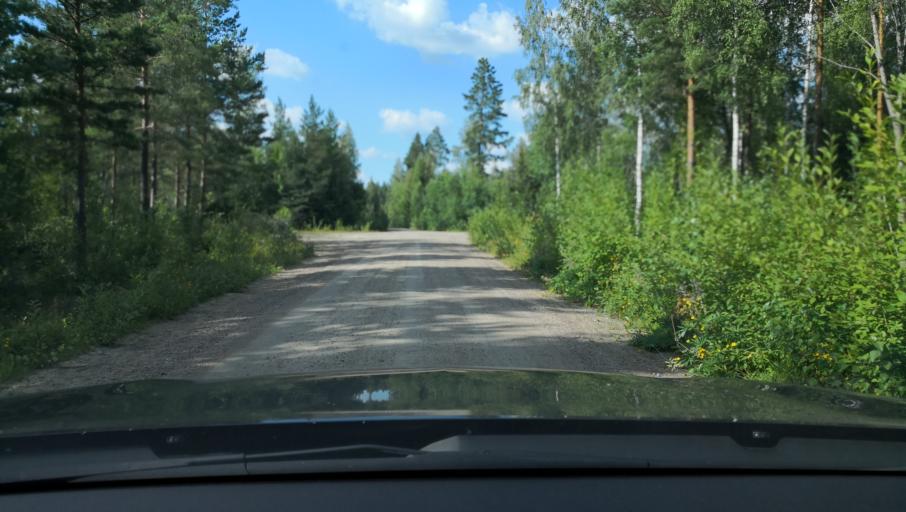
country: SE
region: Vaestmanland
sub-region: Vasteras
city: Skultuna
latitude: 59.7241
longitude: 16.3718
